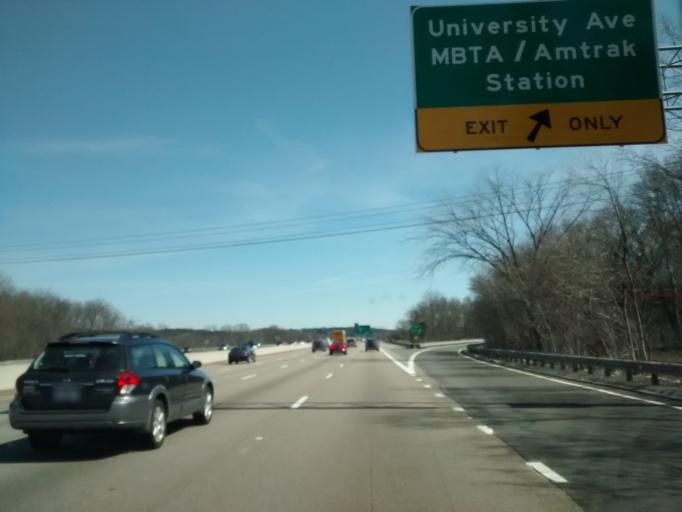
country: US
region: Massachusetts
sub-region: Norfolk County
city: Dedham
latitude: 42.2151
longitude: -71.1538
